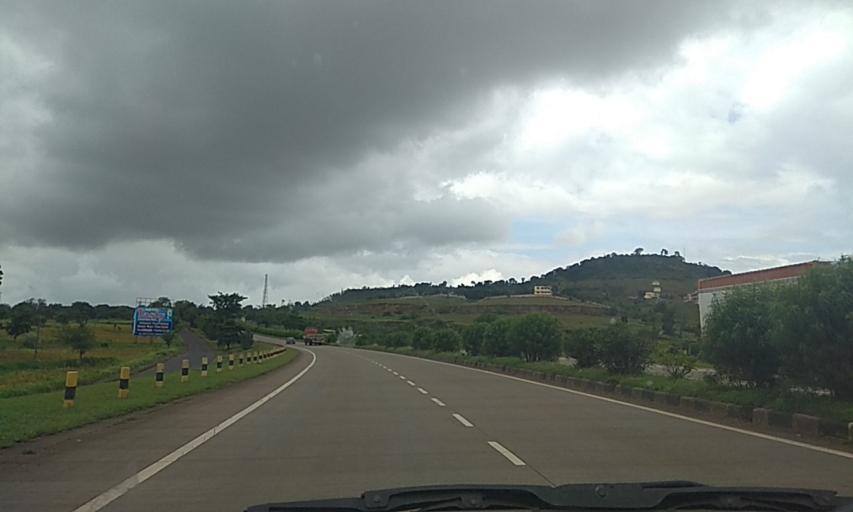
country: IN
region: Karnataka
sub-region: Belgaum
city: Sankeshwar
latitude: 16.2699
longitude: 74.4624
